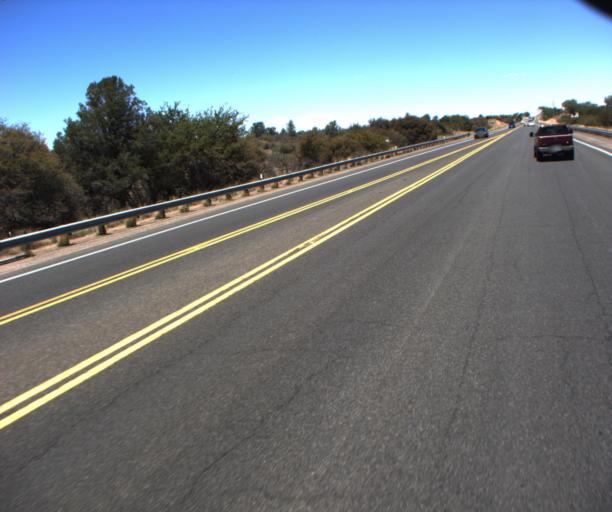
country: US
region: Arizona
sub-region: Yavapai County
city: Prescott
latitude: 34.6344
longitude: -112.4296
